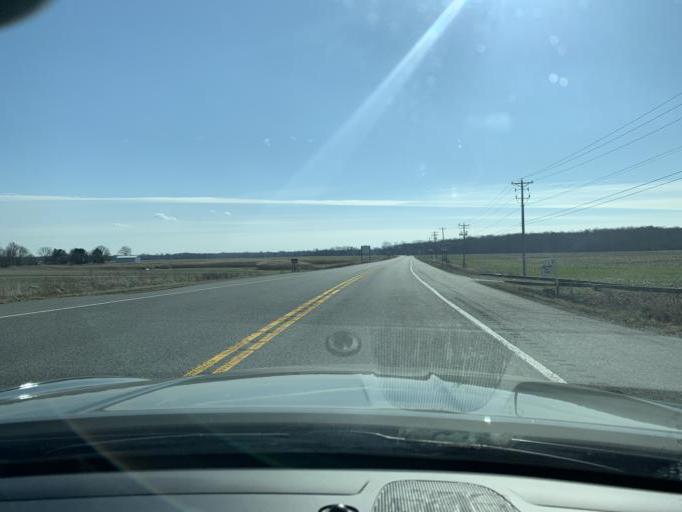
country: US
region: Maryland
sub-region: Queen Anne's County
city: Centreville
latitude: 39.0114
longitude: -76.0756
